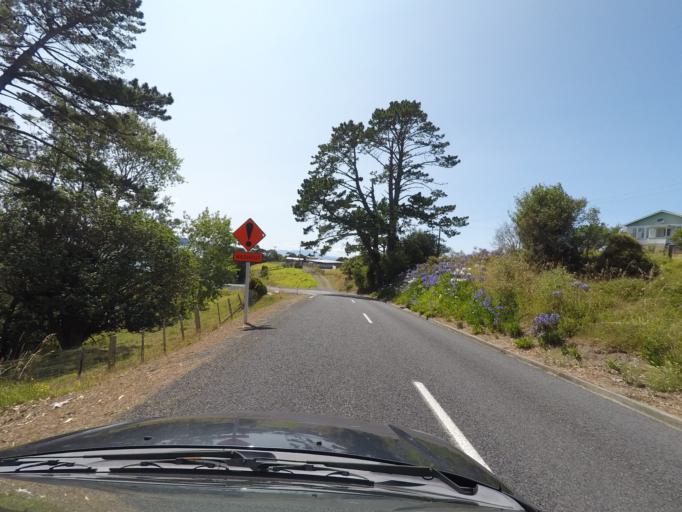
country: NZ
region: Auckland
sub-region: Auckland
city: Warkworth
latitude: -36.4508
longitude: 174.7578
